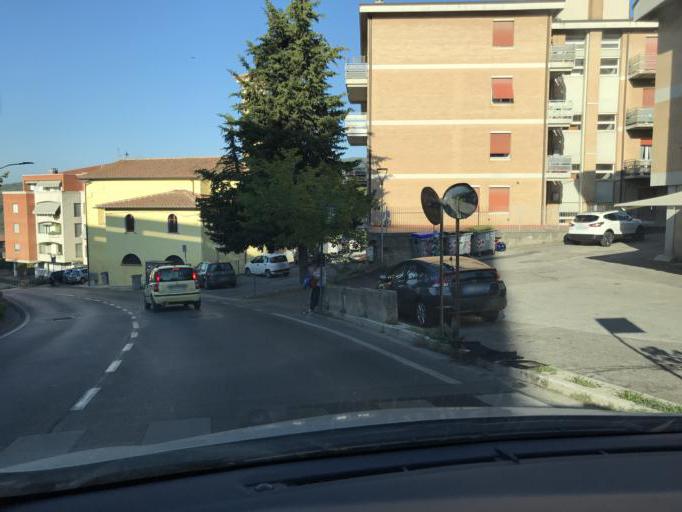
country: IT
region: Umbria
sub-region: Provincia di Perugia
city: Perugia
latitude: 43.1199
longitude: 12.3664
